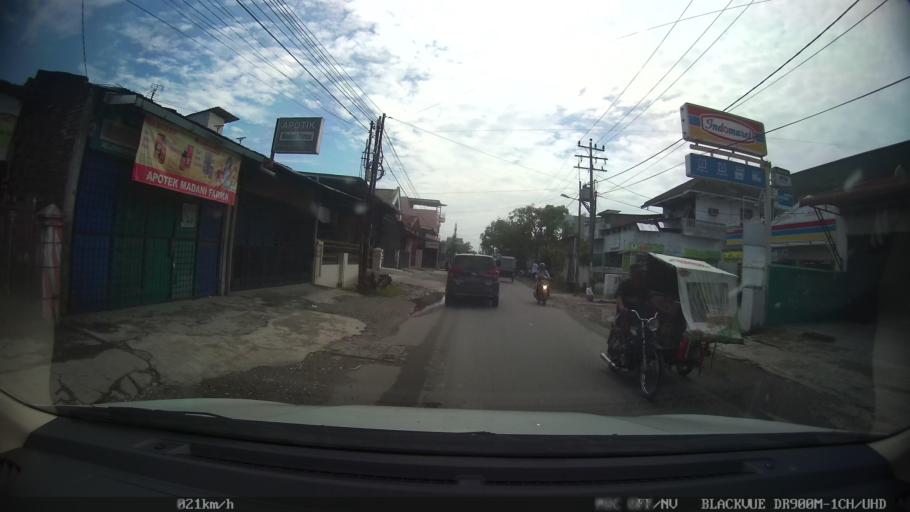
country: ID
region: North Sumatra
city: Medan
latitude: 3.5870
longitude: 98.7271
